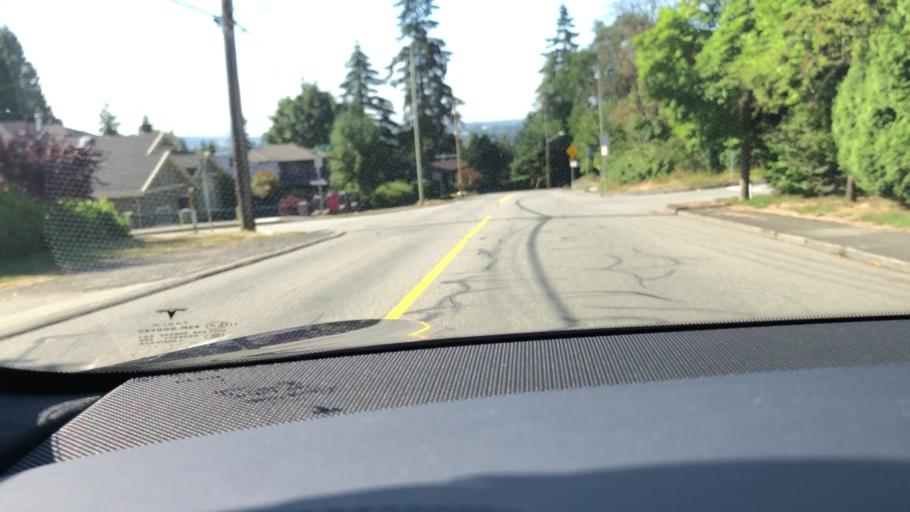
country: CA
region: British Columbia
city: Burnaby
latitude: 49.2123
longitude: -122.9719
